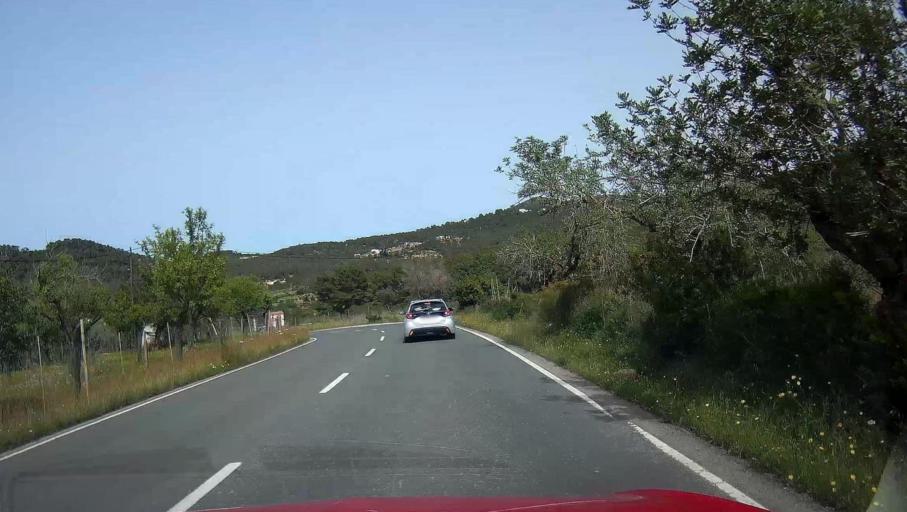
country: ES
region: Balearic Islands
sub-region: Illes Balears
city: Sant Joan de Labritja
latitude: 39.0855
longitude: 1.5006
